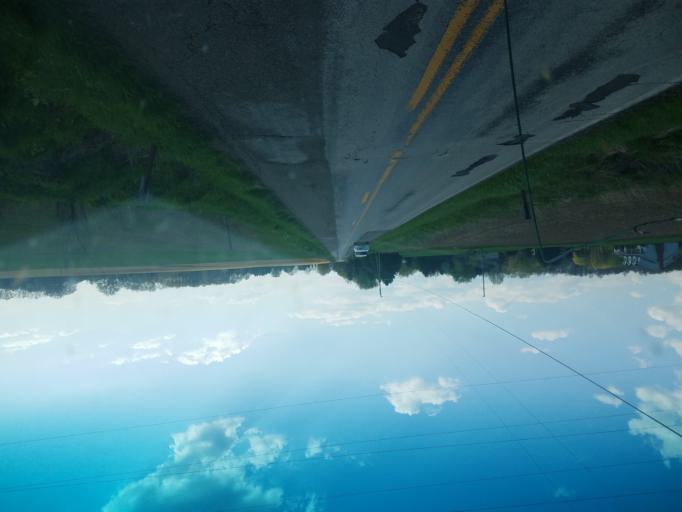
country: US
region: Ohio
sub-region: Wayne County
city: Smithville
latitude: 40.8186
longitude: -81.8646
